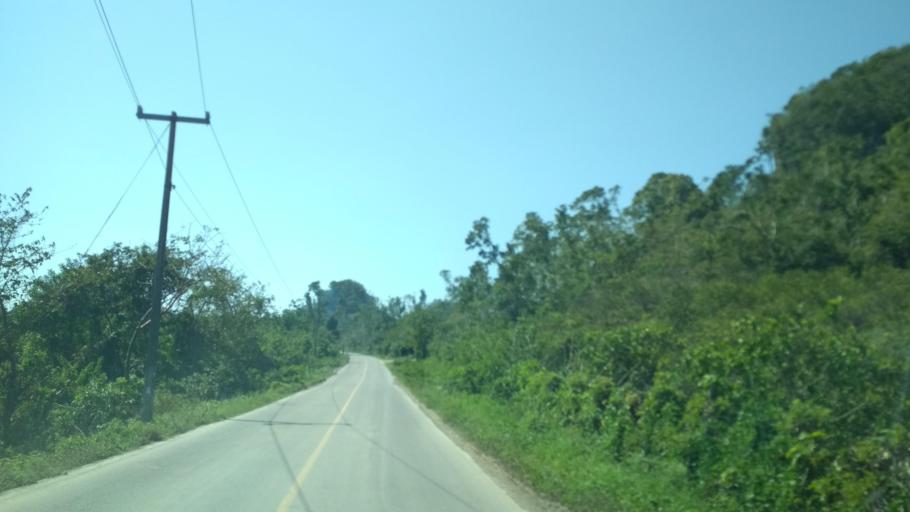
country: MX
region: Veracruz
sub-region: Papantla
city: Polutla
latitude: 20.4717
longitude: -97.2187
